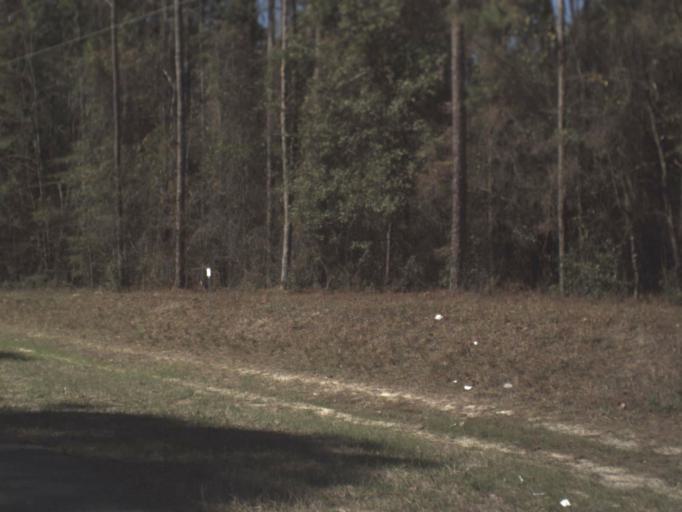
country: US
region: Florida
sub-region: Leon County
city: Woodville
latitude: 30.3082
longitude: -84.3442
